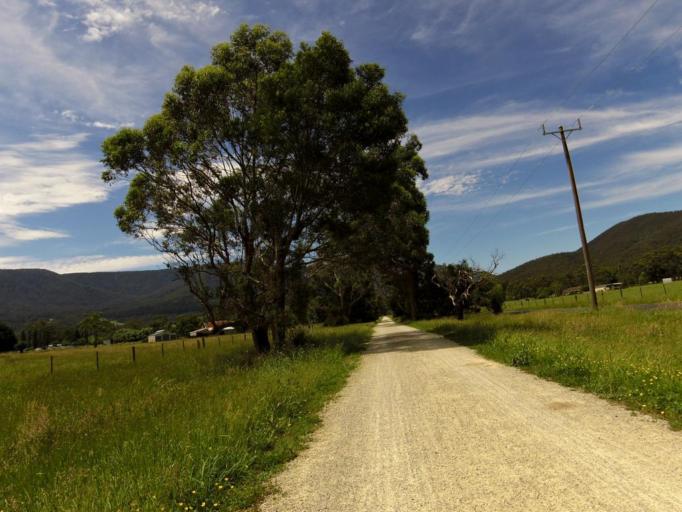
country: AU
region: Victoria
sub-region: Yarra Ranges
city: Yarra Junction
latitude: -37.7697
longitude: 145.6322
